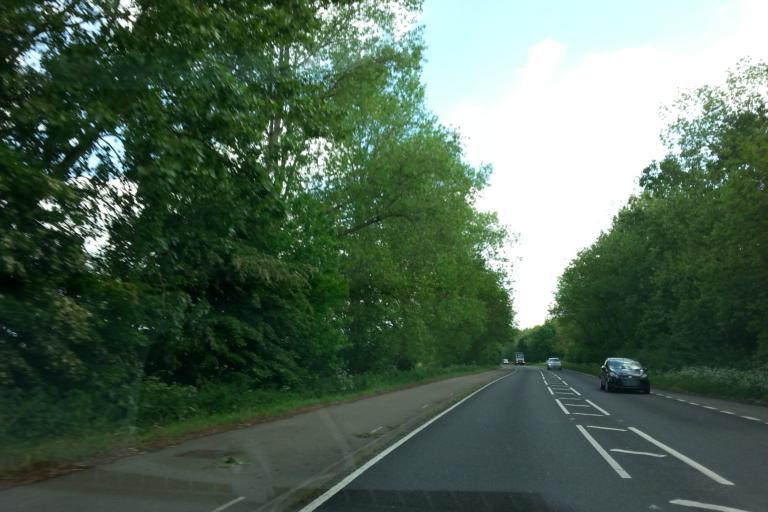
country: GB
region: England
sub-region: Cambridgeshire
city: Yaxley
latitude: 52.5096
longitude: -0.2787
